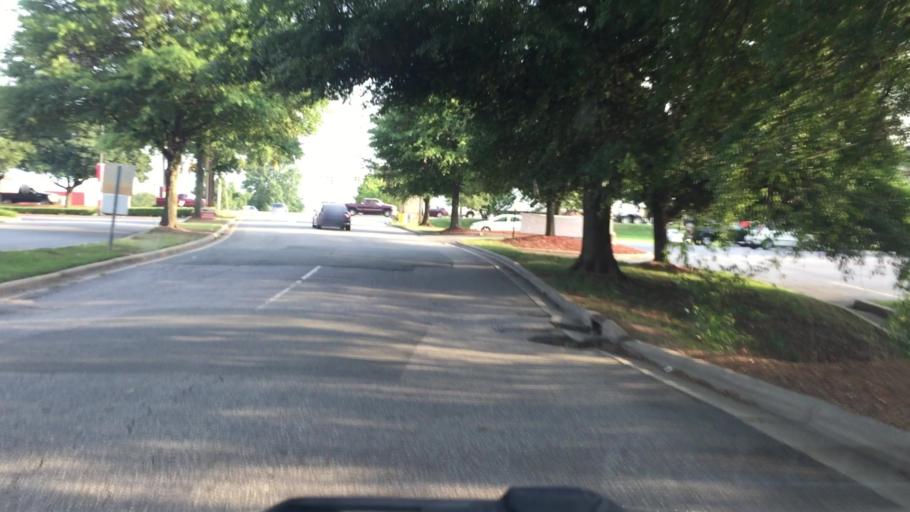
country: US
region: North Carolina
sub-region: Iredell County
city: Mooresville
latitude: 35.5945
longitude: -80.8562
